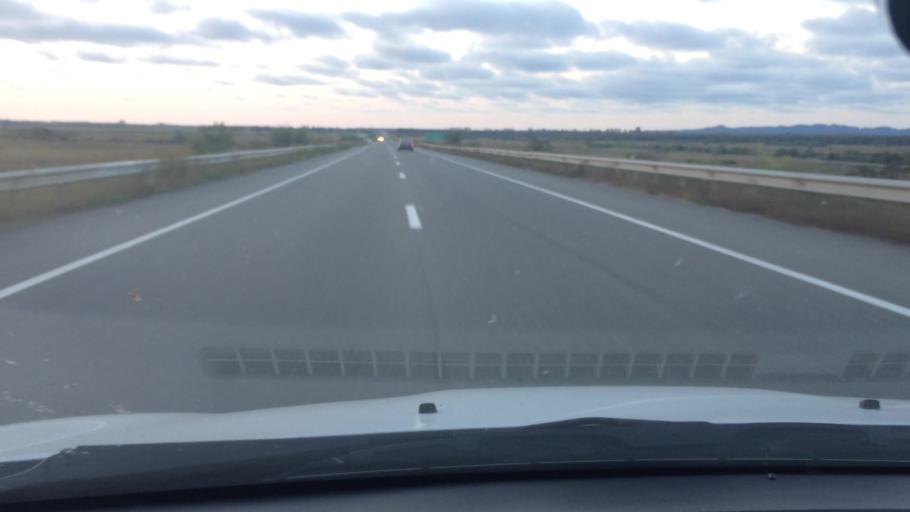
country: GE
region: Ajaria
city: Ochkhamuri
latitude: 41.8694
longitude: 41.8325
